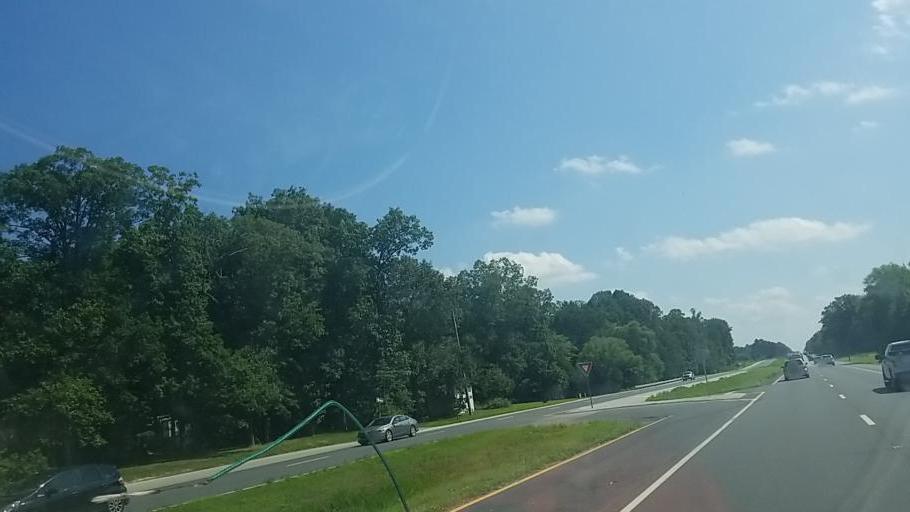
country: US
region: Delaware
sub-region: Sussex County
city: Milford
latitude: 38.8806
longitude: -75.4396
